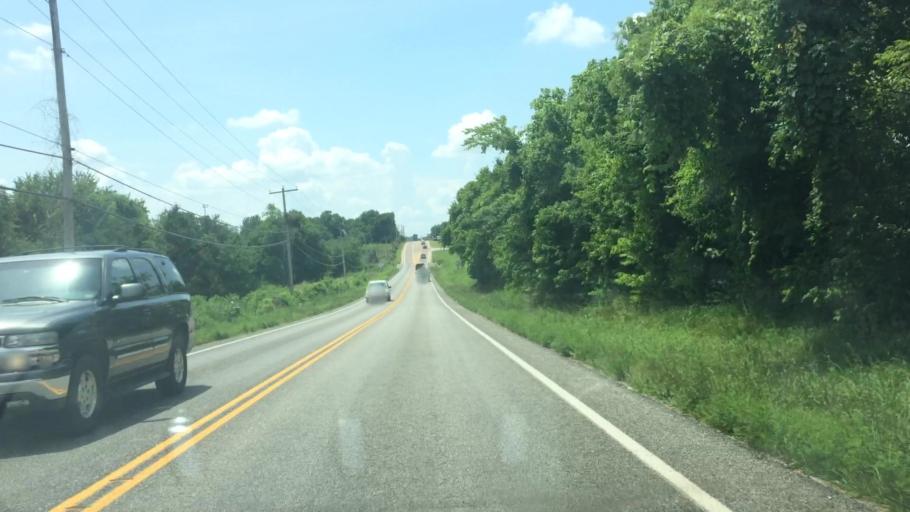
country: US
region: Missouri
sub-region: Greene County
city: Springfield
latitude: 37.2695
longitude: -93.2646
